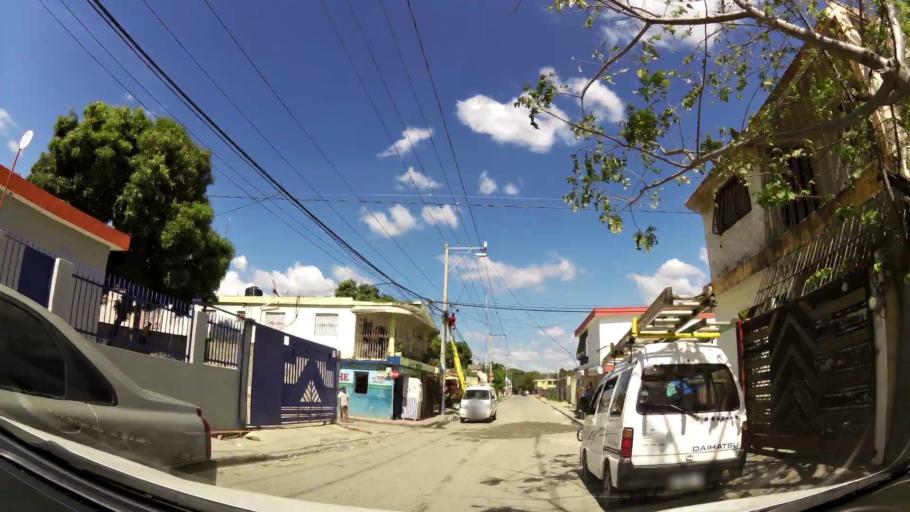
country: DO
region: San Cristobal
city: San Cristobal
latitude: 18.4237
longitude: -70.1002
